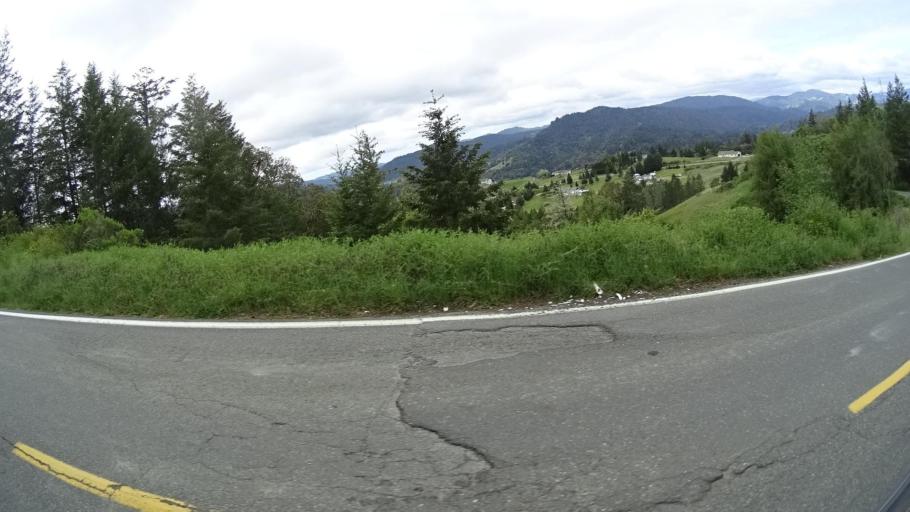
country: US
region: California
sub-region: Humboldt County
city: Redway
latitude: 40.1103
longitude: -123.7797
